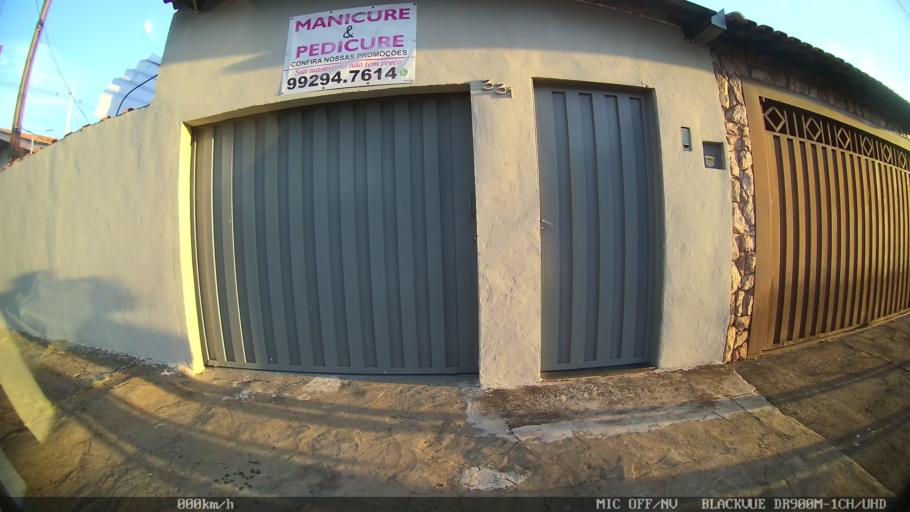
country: BR
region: Sao Paulo
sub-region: Franca
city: Franca
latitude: -20.5183
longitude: -47.4090
